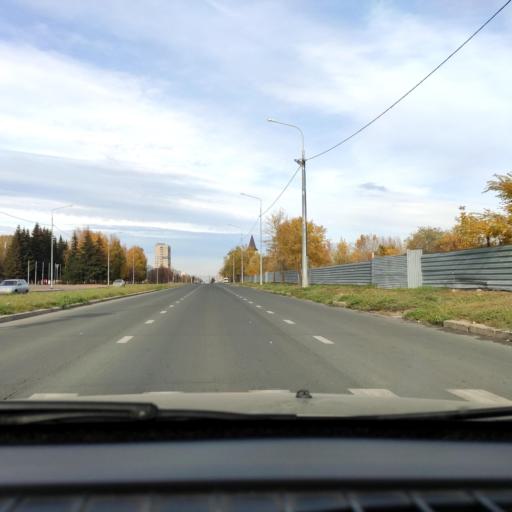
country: RU
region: Samara
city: Tol'yatti
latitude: 53.5023
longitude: 49.2698
